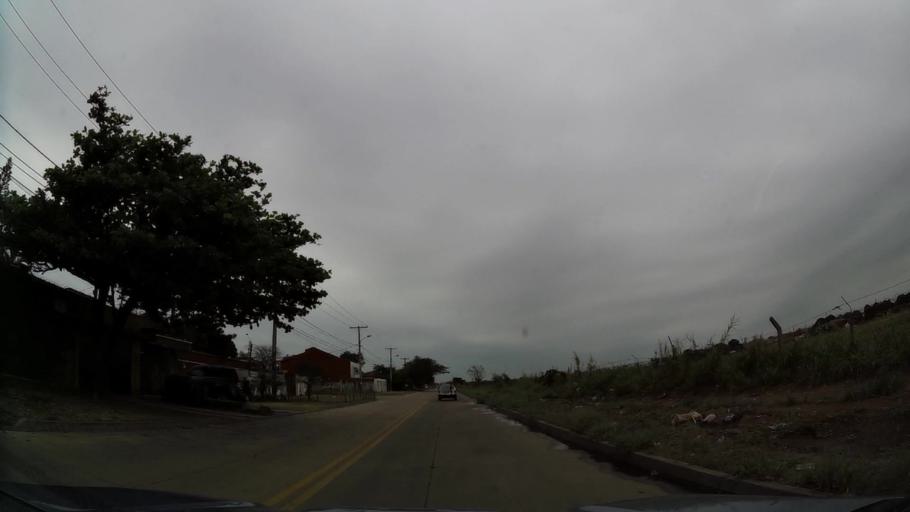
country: BO
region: Santa Cruz
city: Santa Cruz de la Sierra
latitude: -17.8132
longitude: -63.1689
